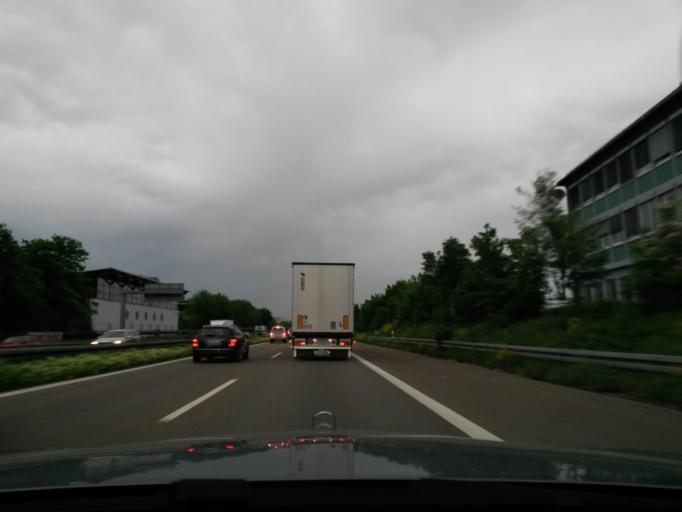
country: DE
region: Baden-Wuerttemberg
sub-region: Regierungsbezirk Stuttgart
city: Stuttgart-Ost
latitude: 48.7714
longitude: 9.2497
